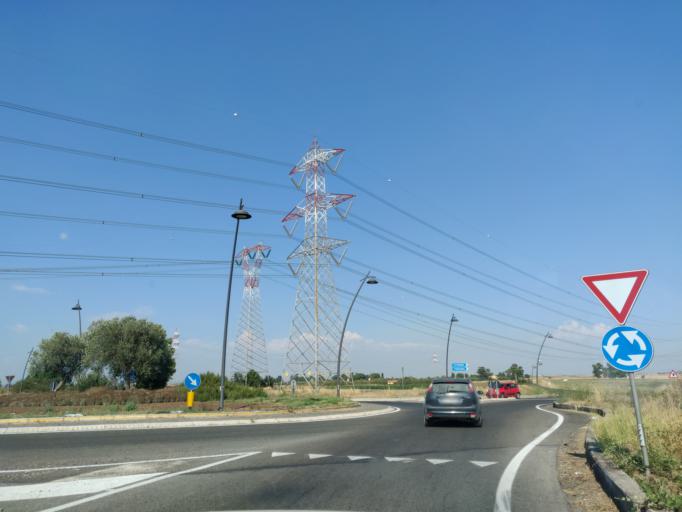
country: IT
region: Latium
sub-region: Provincia di Viterbo
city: Montalto di Castro
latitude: 42.3599
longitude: 11.6437
